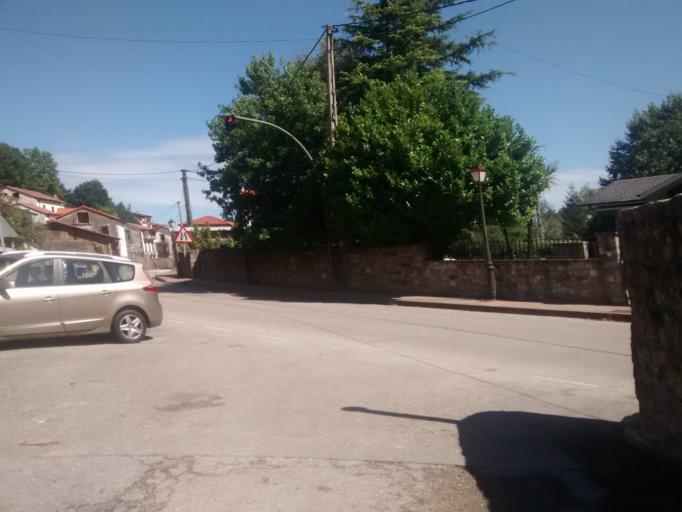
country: ES
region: Cantabria
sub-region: Provincia de Cantabria
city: Lierganes
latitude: 43.3392
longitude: -3.7445
